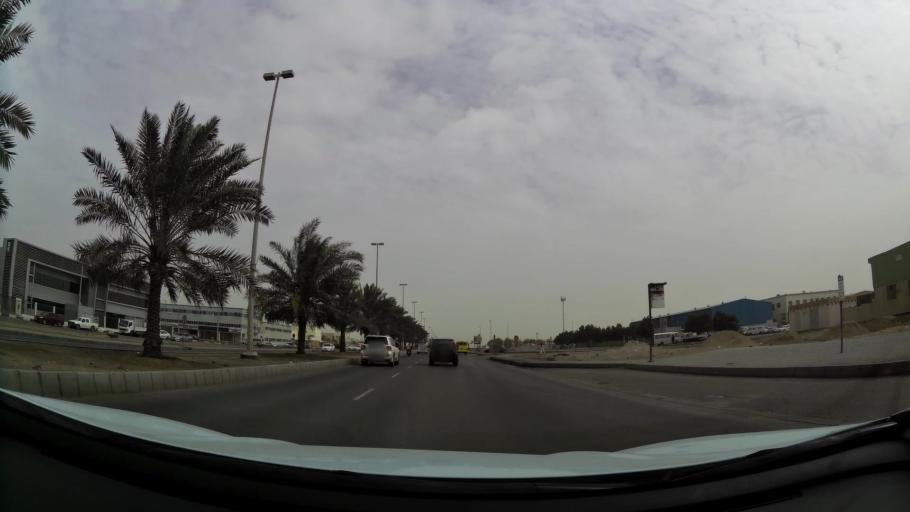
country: AE
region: Abu Dhabi
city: Abu Dhabi
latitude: 24.3456
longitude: 54.5001
